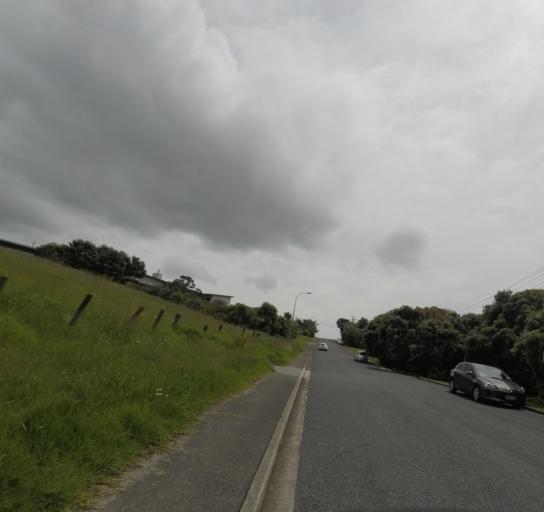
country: NZ
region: Auckland
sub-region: Auckland
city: Warkworth
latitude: -36.2962
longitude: 174.8027
